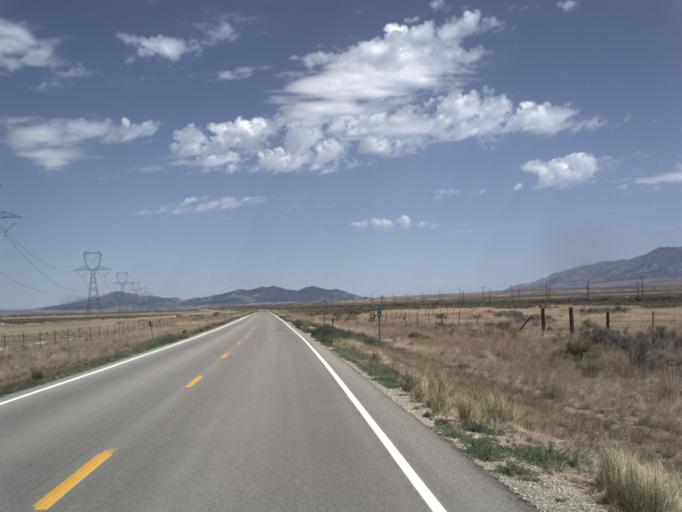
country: US
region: Utah
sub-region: Tooele County
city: Tooele
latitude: 40.2660
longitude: -112.3974
